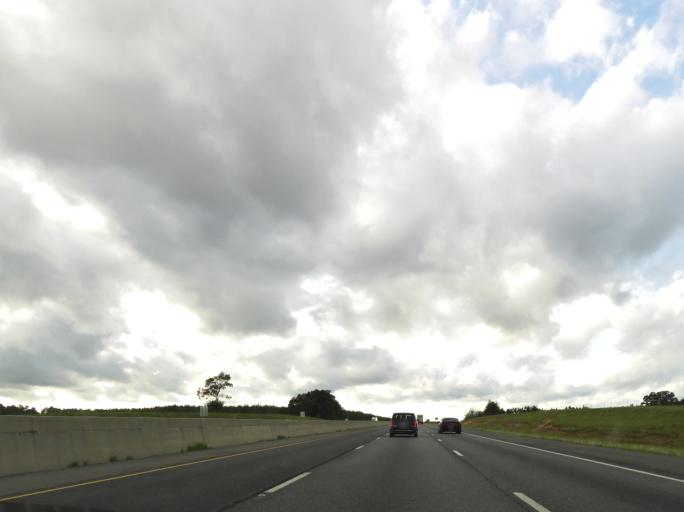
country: US
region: Georgia
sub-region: Turner County
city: Ashburn
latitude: 31.8020
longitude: -83.7022
